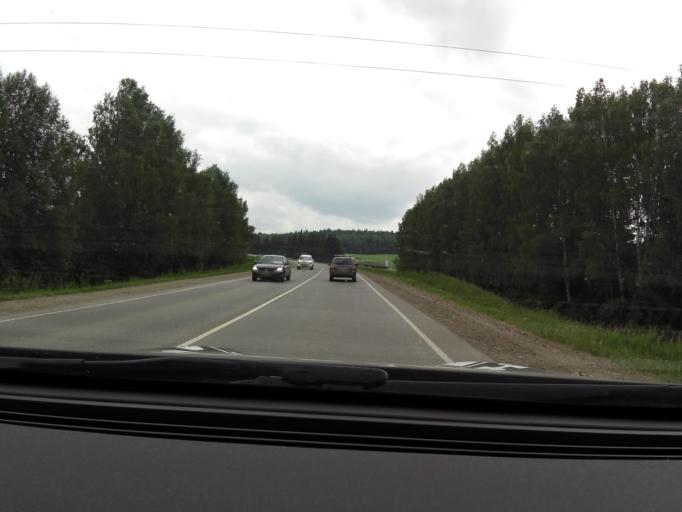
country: RU
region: Perm
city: Kukushtan
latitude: 57.4874
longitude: 56.6681
